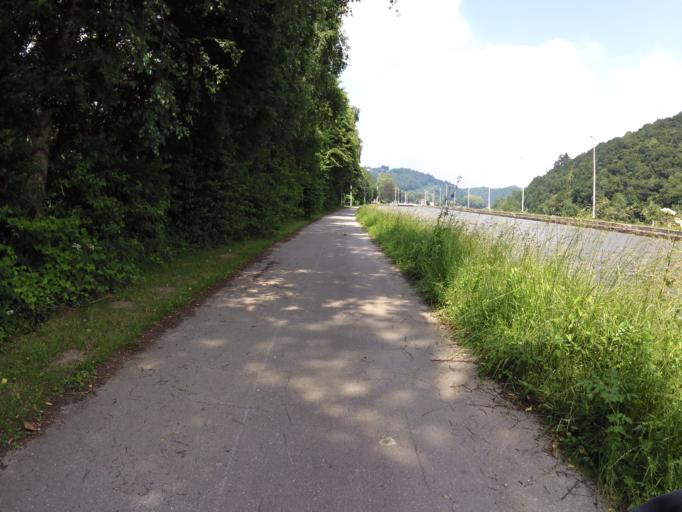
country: BE
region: Wallonia
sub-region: Province de Namur
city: Hastiere-Lavaux
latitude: 50.2001
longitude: 4.8184
